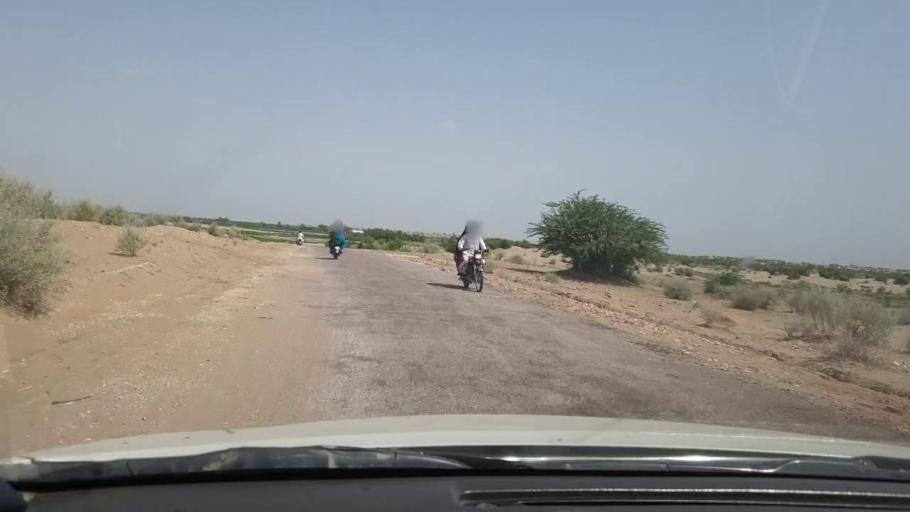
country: PK
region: Sindh
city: Rohri
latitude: 27.4898
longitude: 69.0521
